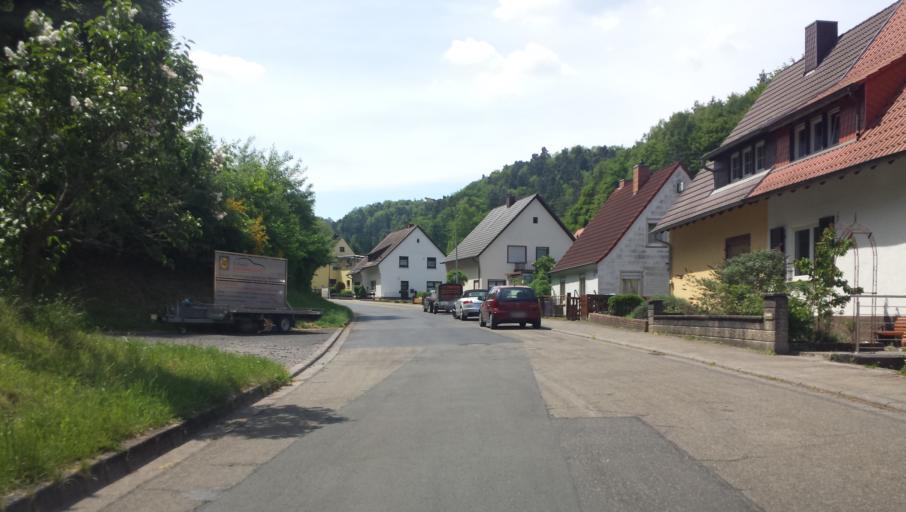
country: DE
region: Rheinland-Pfalz
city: Frankenstein
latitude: 49.4169
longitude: 7.9776
